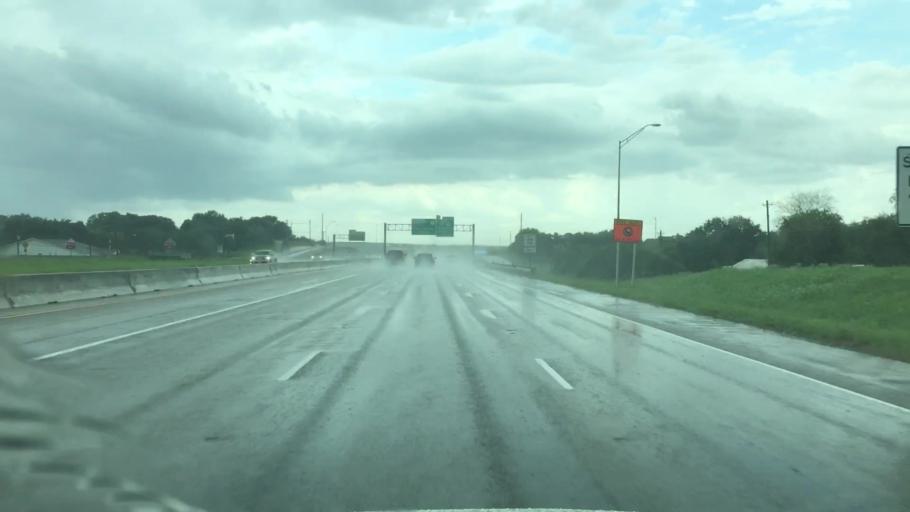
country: US
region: Texas
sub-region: Nueces County
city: Robstown
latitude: 27.8587
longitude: -97.6066
